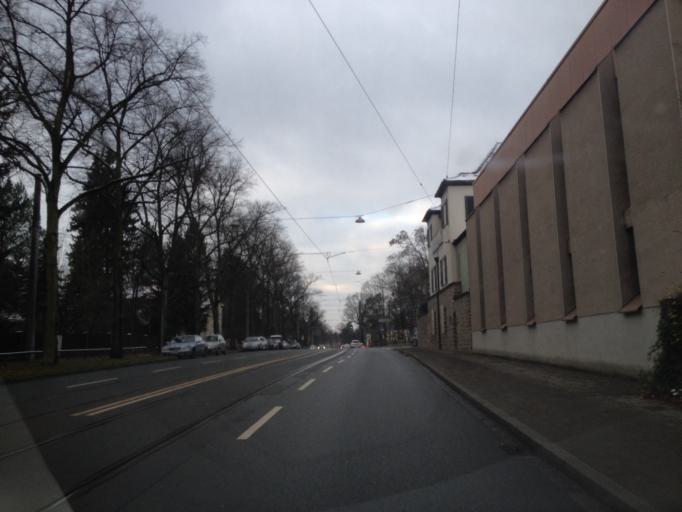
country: DE
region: Bavaria
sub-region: Regierungsbezirk Mittelfranken
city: Nuernberg
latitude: 49.4703
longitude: 11.1318
